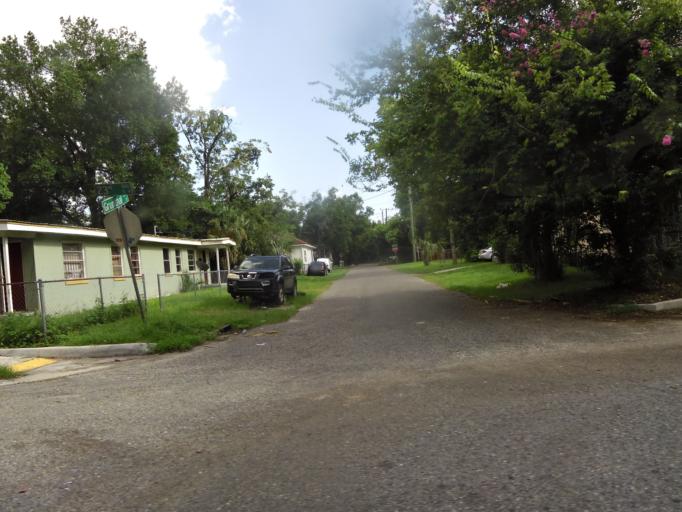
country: US
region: Florida
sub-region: Duval County
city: Jacksonville
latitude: 30.3581
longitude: -81.6829
